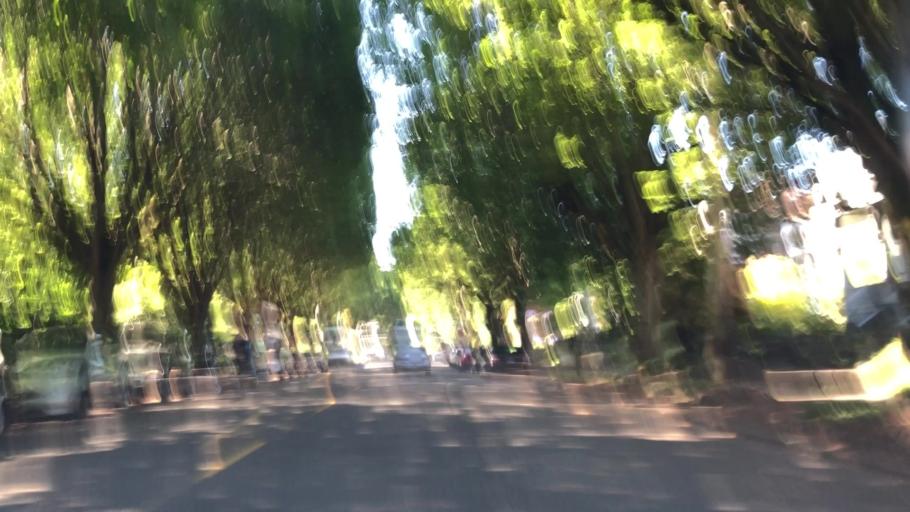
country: US
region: Washington
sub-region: King County
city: Seattle
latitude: 47.6300
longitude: -122.3073
